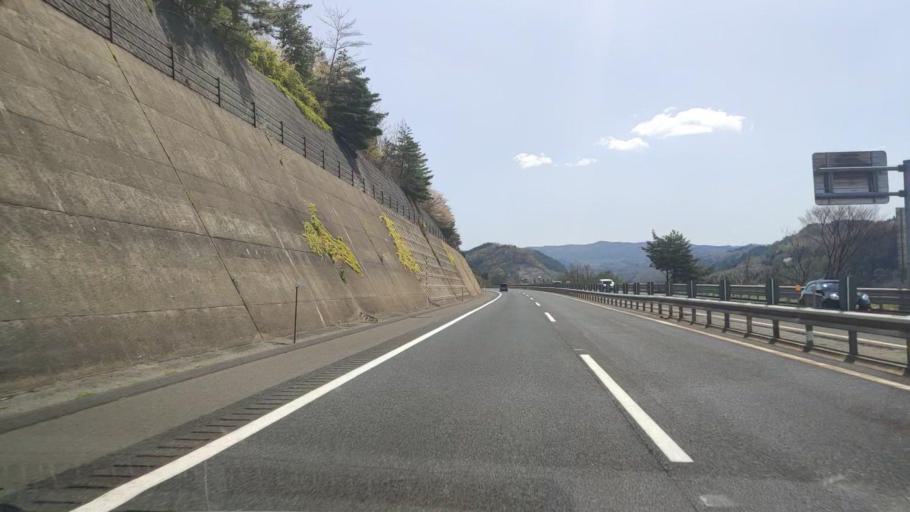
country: JP
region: Iwate
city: Ichinohe
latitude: 40.2308
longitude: 141.3136
